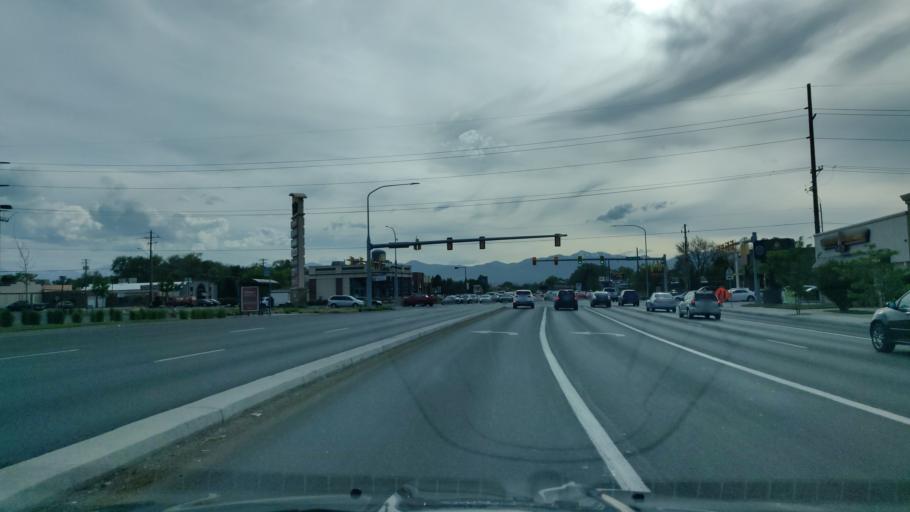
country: US
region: Utah
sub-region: Salt Lake County
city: Sandy City
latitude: 40.6223
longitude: -111.8649
